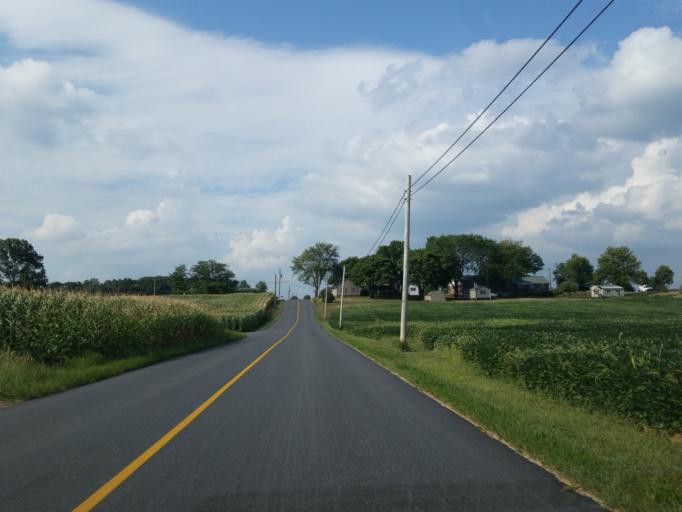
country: US
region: Pennsylvania
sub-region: Lancaster County
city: Manheim
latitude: 40.1618
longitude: -76.4562
